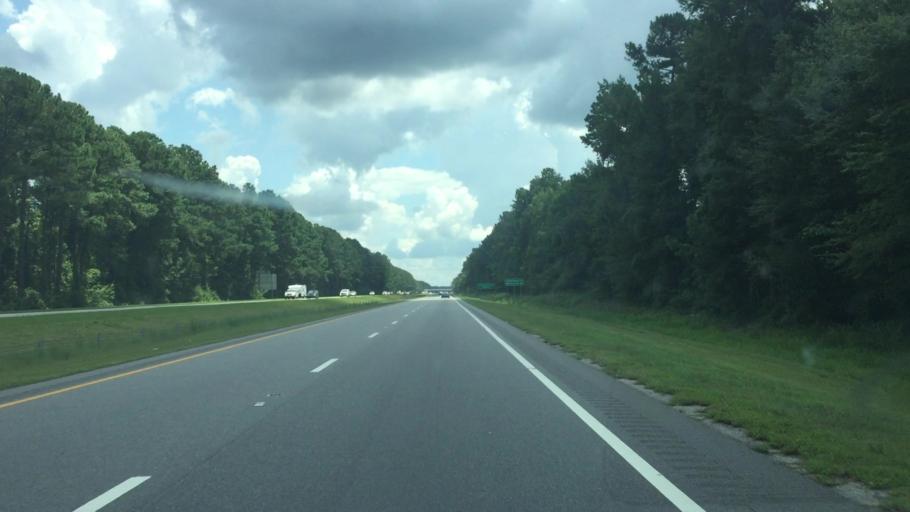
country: US
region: North Carolina
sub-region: Columbus County
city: Chadbourn
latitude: 34.3923
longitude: -78.8884
